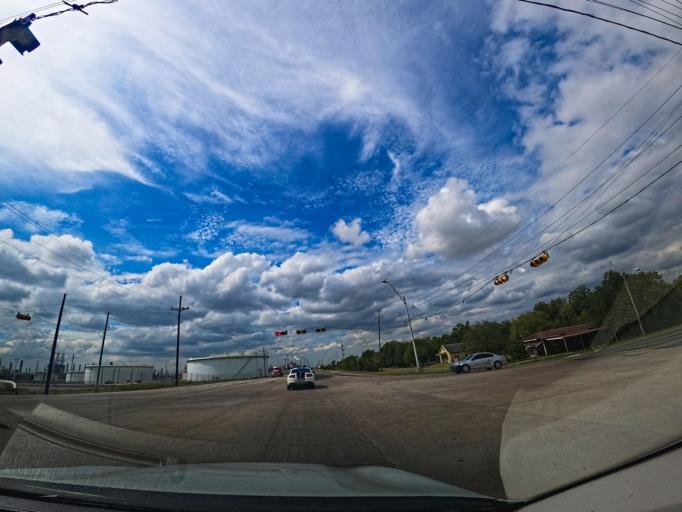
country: US
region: Texas
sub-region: Jefferson County
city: Port Arthur
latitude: 29.8583
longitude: -93.9516
